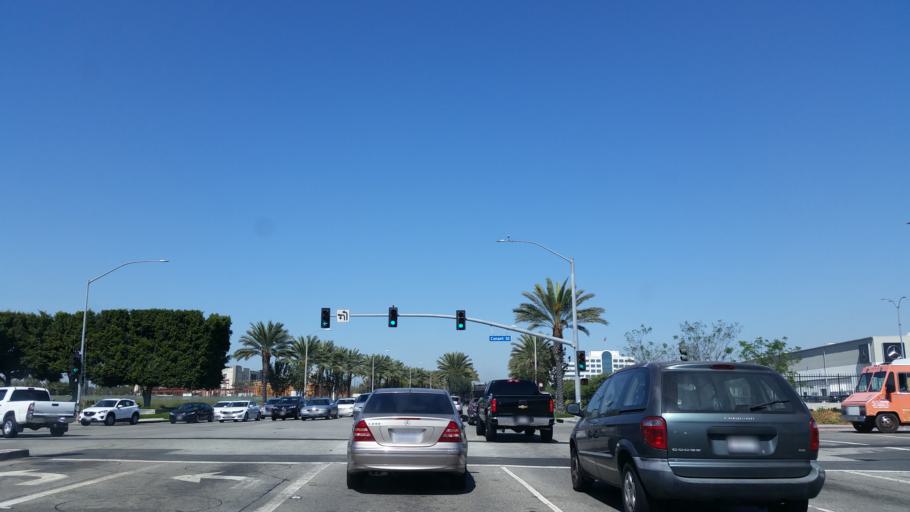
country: US
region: California
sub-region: Los Angeles County
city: Lakewood
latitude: 33.8248
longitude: -118.1425
